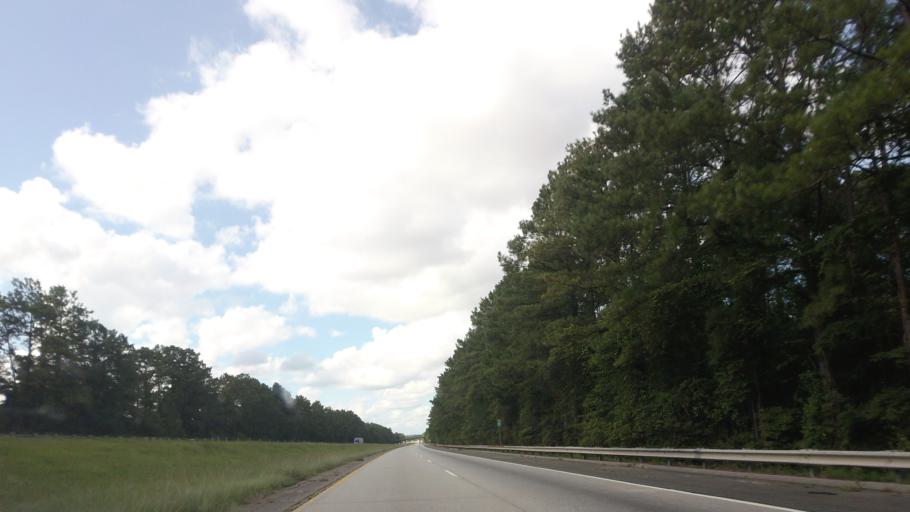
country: US
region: Georgia
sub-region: Bibb County
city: Macon
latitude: 32.7670
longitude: -83.5565
